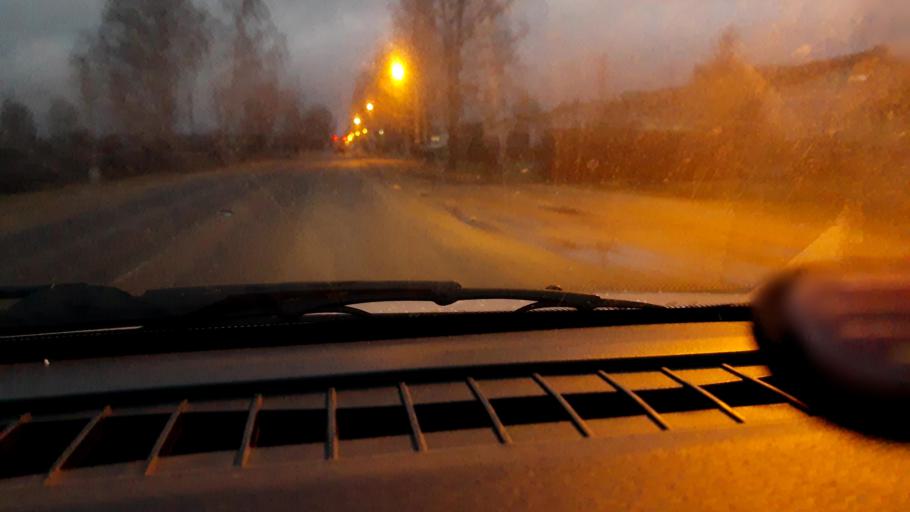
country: RU
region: Nizjnij Novgorod
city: Uren'
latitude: 57.4460
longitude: 45.7346
